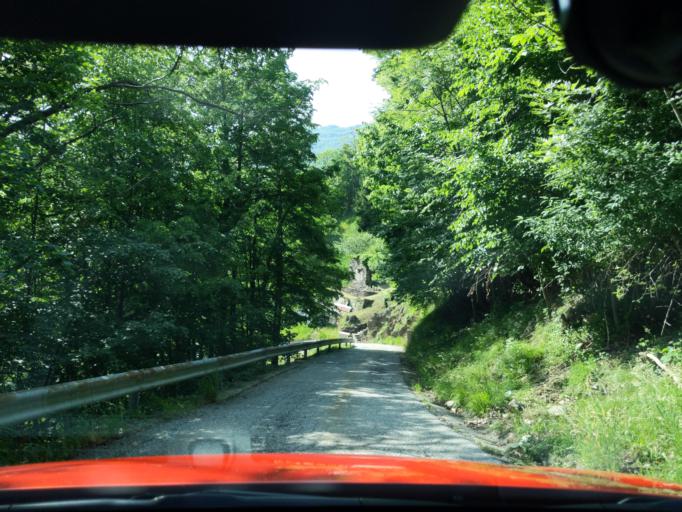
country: IT
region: Piedmont
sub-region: Provincia Verbano-Cusio-Ossola
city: Falmenta
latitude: 46.0903
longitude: 8.5967
